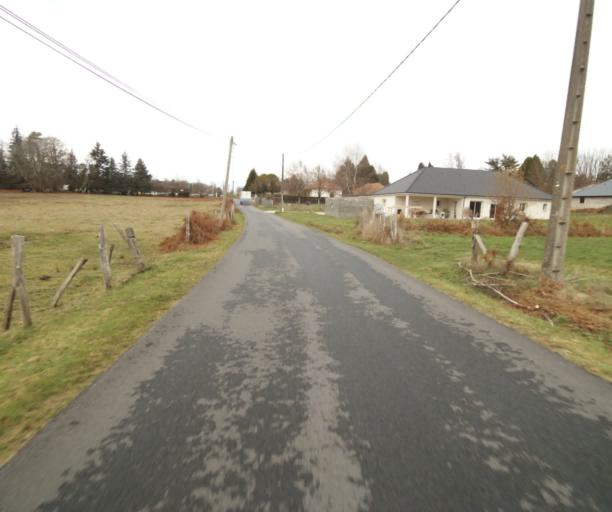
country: FR
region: Limousin
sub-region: Departement de la Correze
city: Saint-Mexant
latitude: 45.2684
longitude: 1.6674
